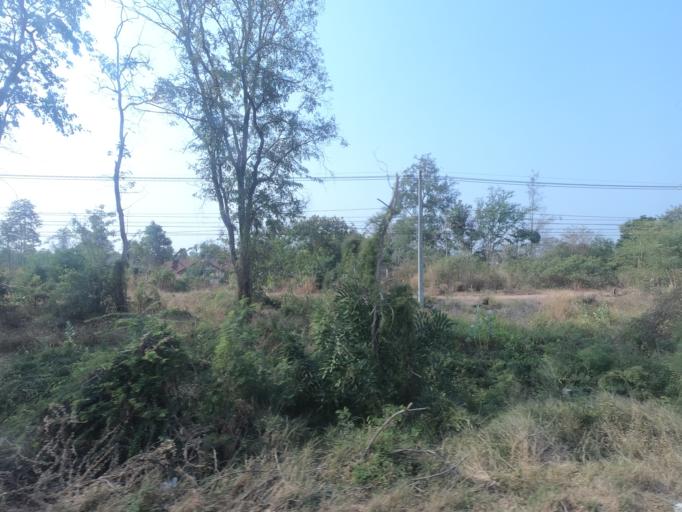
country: TH
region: Khon Kaen
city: Non Sila
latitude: 15.9065
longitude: 102.6552
